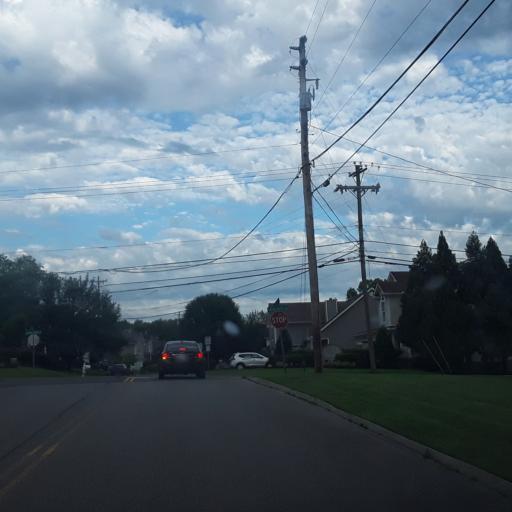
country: US
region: Tennessee
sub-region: Wilson County
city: Green Hill
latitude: 36.1642
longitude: -86.5854
